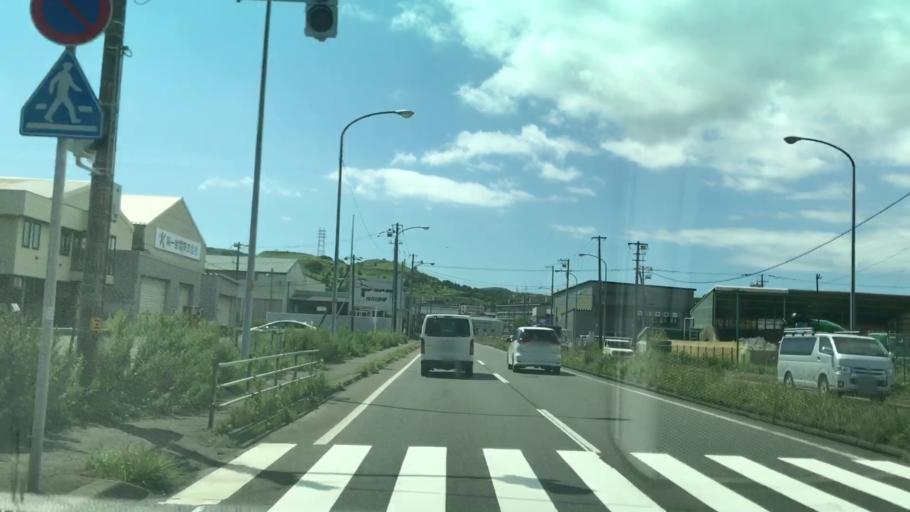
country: JP
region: Hokkaido
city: Muroran
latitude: 42.3387
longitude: 141.0259
